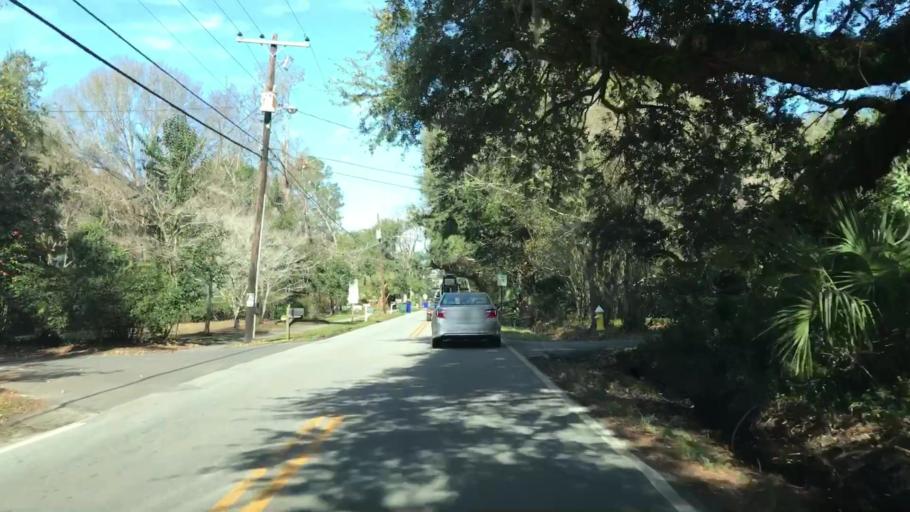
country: US
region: South Carolina
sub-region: Charleston County
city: North Charleston
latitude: 32.7796
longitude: -80.0196
